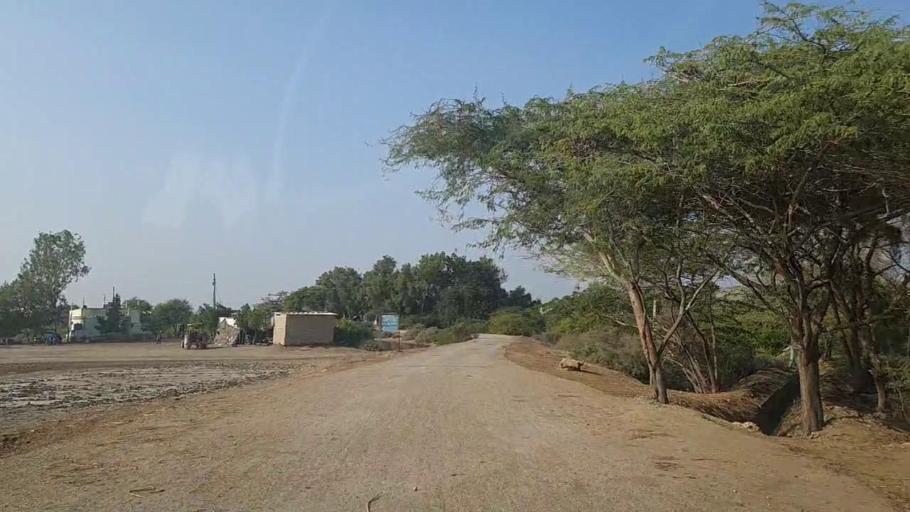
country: PK
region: Sindh
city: Mirpur Sakro
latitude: 24.5727
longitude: 67.6660
